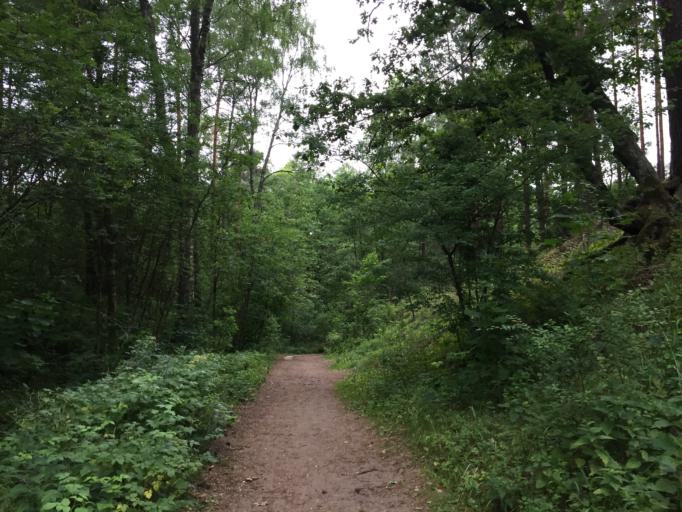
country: LV
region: Carnikava
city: Carnikava
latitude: 57.1192
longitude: 24.2225
